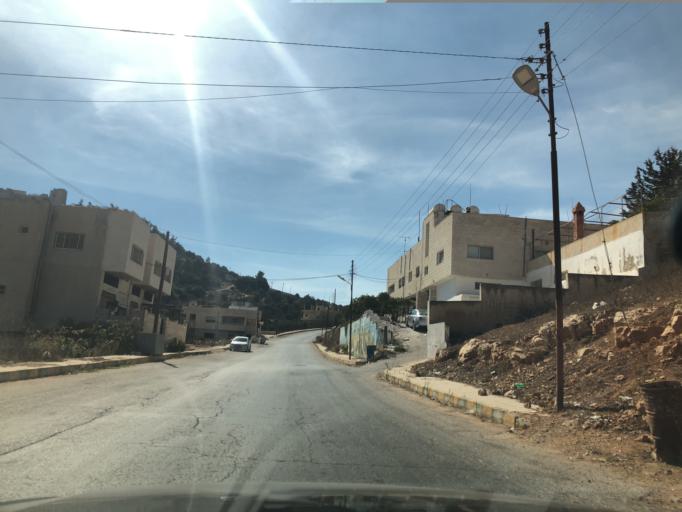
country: JO
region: Ajlun
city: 'Ajlun
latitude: 32.3285
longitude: 35.7307
